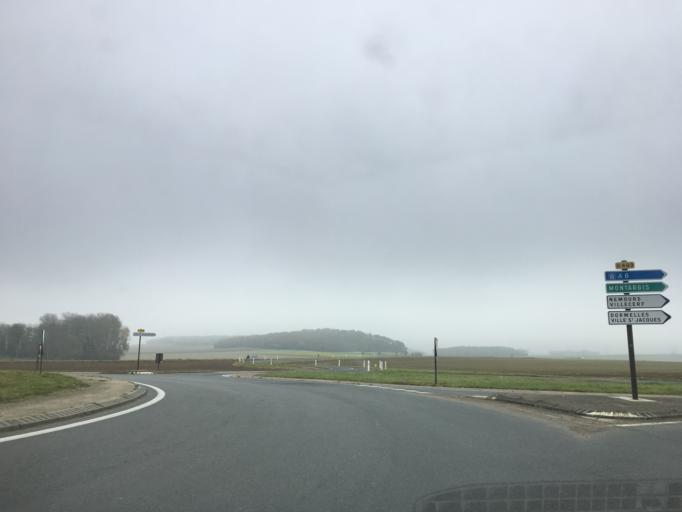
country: FR
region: Ile-de-France
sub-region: Departement de Seine-et-Marne
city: Varennes-sur-Seine
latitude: 48.3608
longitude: 2.9299
